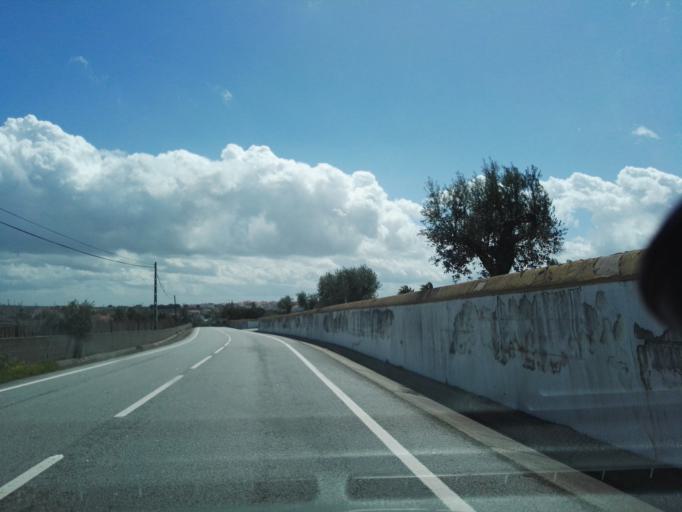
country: PT
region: Portalegre
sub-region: Arronches
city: Arronches
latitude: 39.1301
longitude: -7.2855
